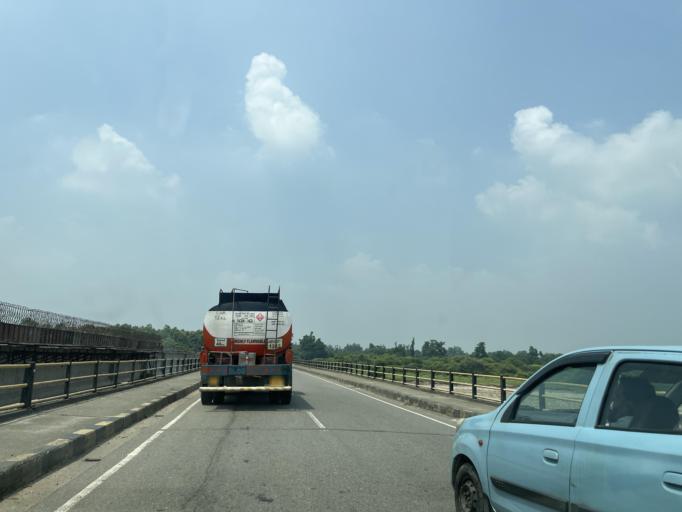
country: IN
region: Uttarakhand
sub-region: Haridwar
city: Haridwar
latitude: 29.8402
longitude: 78.1935
